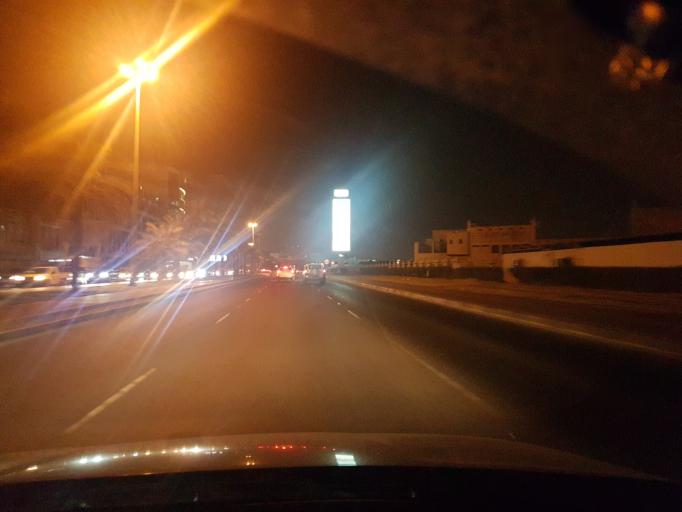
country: BH
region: Manama
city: Manama
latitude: 26.2134
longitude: 50.5968
